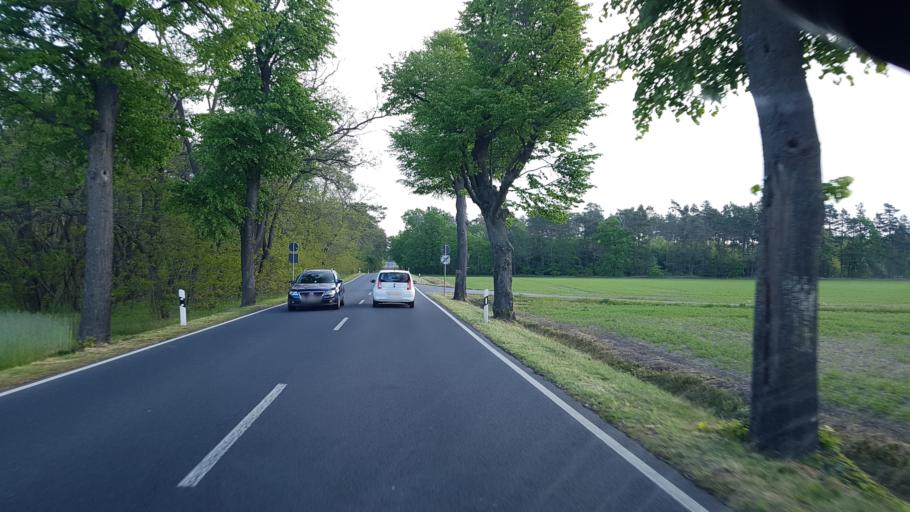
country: DE
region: Brandenburg
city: Sonnewalde
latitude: 51.7230
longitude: 13.6743
